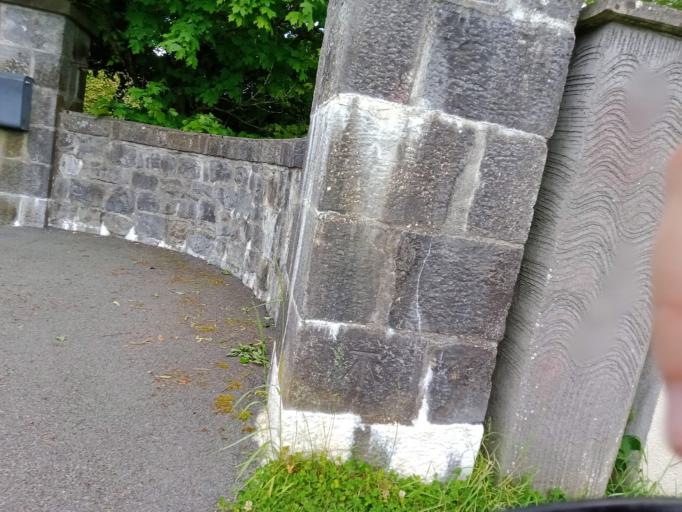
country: IE
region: Leinster
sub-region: Kilkenny
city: Kilkenny
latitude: 52.6877
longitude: -7.2491
